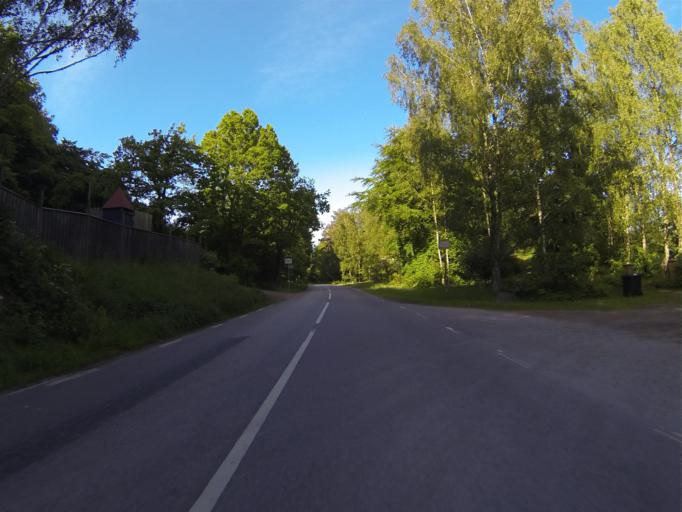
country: SE
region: Skane
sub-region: Lunds Kommun
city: Genarp
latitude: 55.6722
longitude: 13.4096
